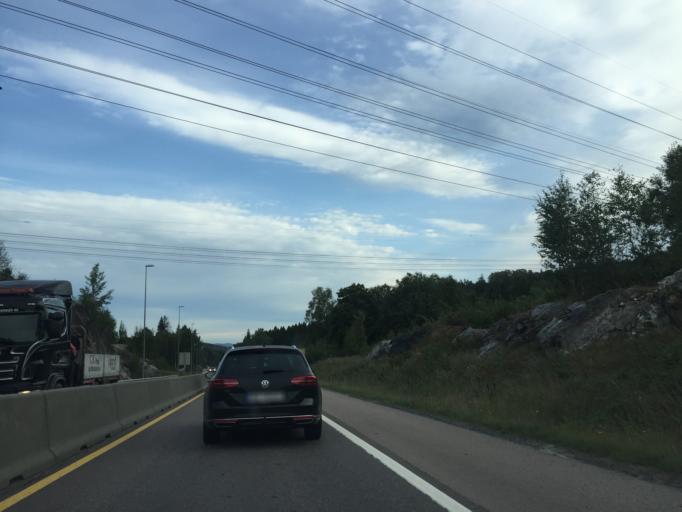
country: NO
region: Akershus
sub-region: Ski
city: Ski
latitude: 59.7282
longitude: 10.7854
